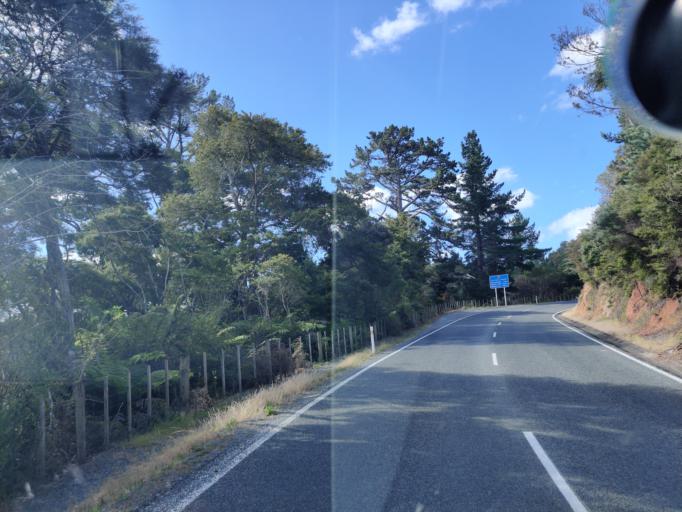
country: NZ
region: Northland
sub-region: Whangarei
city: Ngunguru
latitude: -35.6072
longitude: 174.5234
